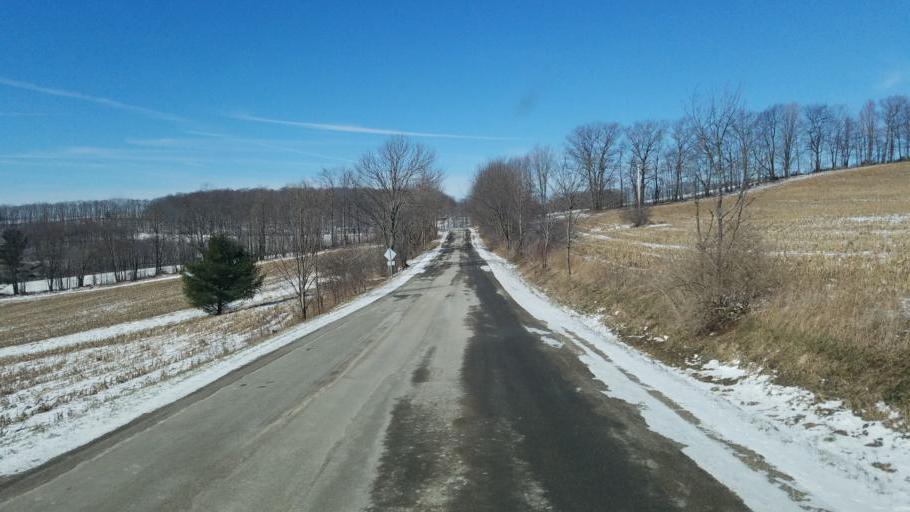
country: US
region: New York
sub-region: Allegany County
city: Wellsville
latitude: 42.0842
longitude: -77.9922
